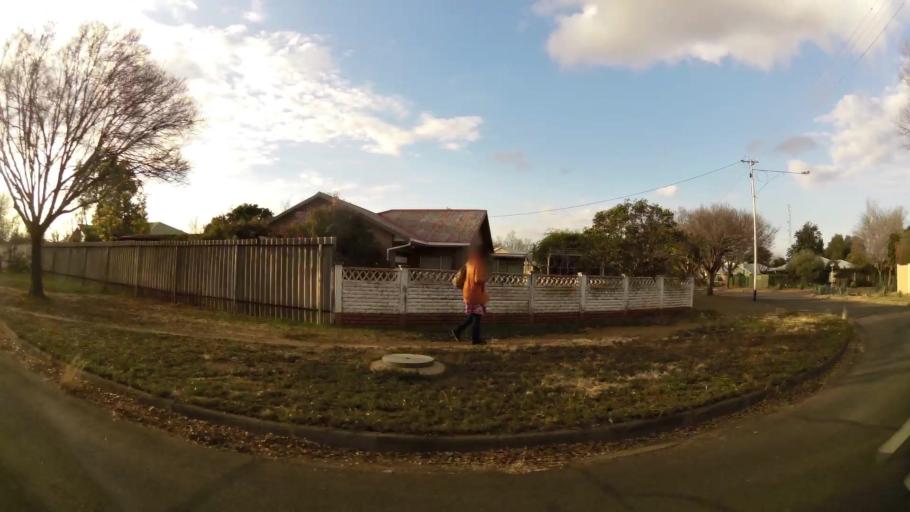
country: ZA
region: Orange Free State
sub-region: Mangaung Metropolitan Municipality
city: Bloemfontein
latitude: -29.1405
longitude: 26.1970
